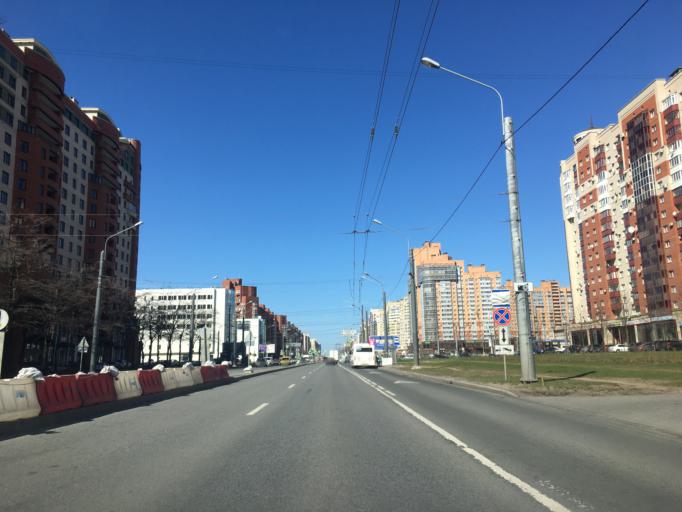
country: RU
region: St.-Petersburg
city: Uritsk
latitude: 59.8554
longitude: 30.2060
